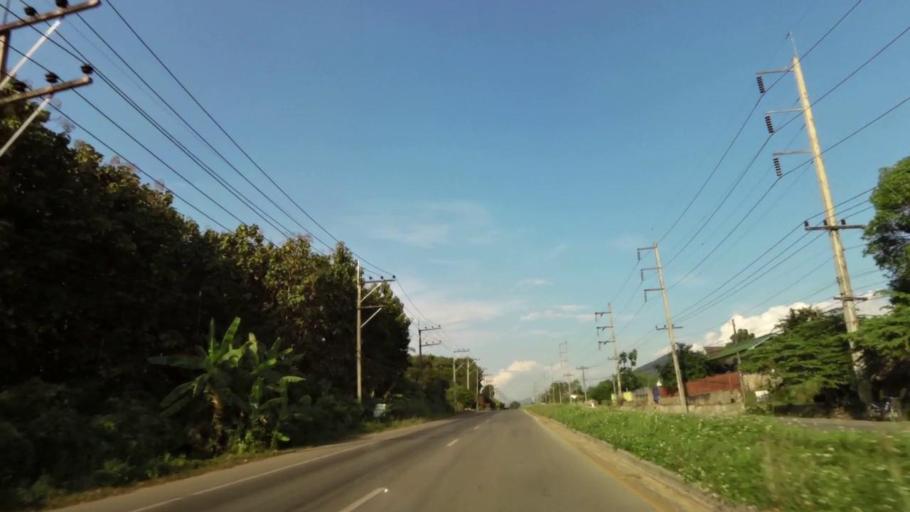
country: TH
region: Chiang Rai
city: Khun Tan
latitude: 19.8739
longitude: 100.2872
